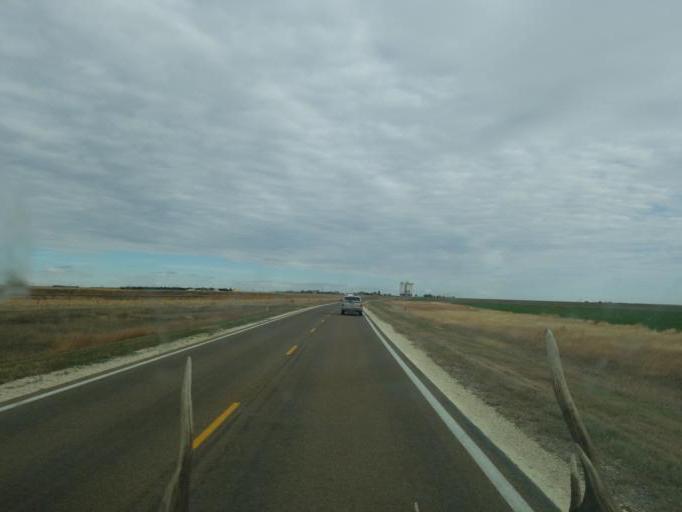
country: US
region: Kansas
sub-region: Logan County
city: Oakley
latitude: 39.0846
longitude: -101.1702
